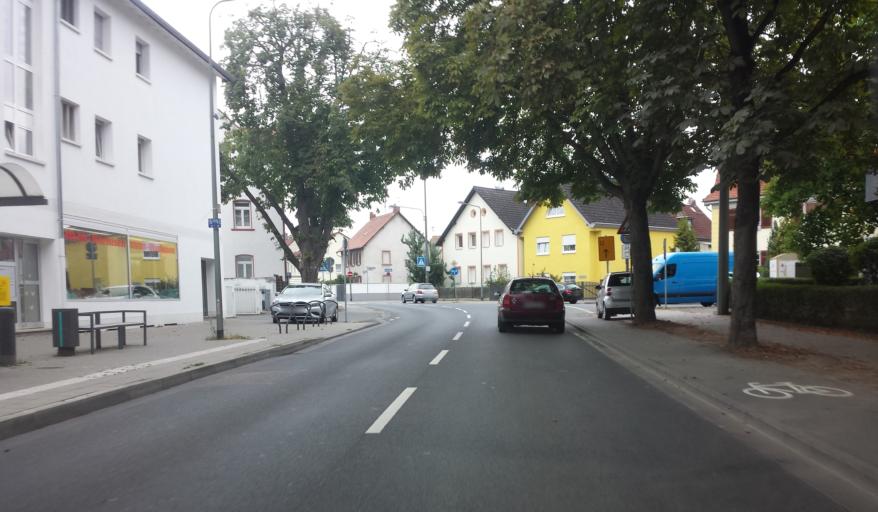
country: DE
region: Hesse
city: Liederbach
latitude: 50.0971
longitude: 8.4942
